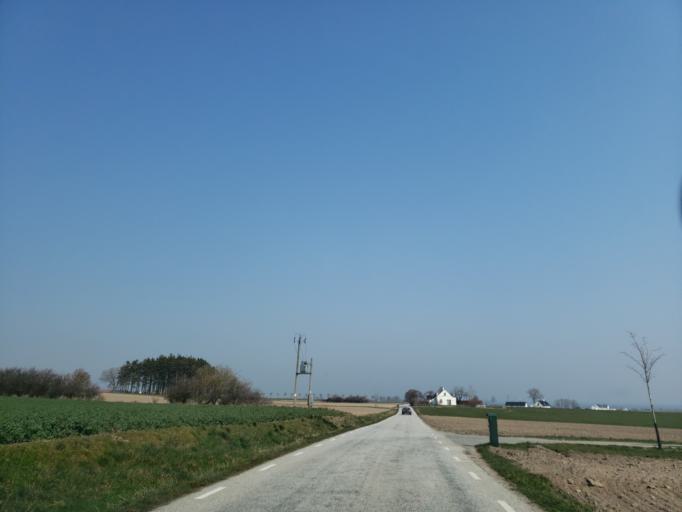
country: SE
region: Skane
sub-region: Simrishamns Kommun
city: Simrishamn
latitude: 55.5083
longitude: 14.3156
